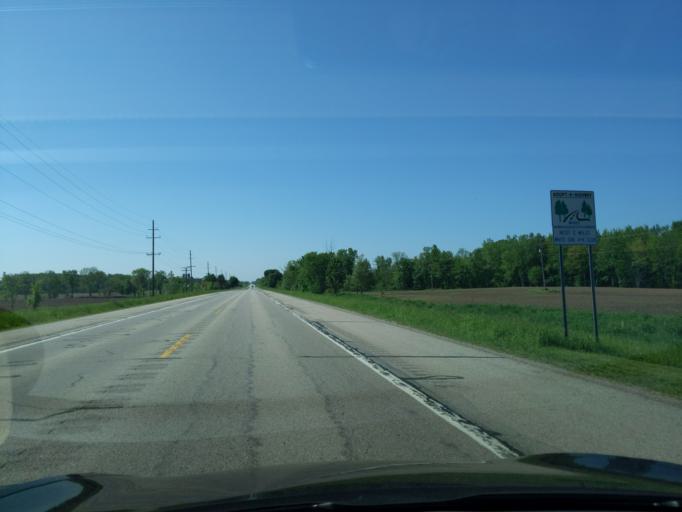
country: US
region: Michigan
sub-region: Ingham County
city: Webberville
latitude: 42.5687
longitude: -84.1921
